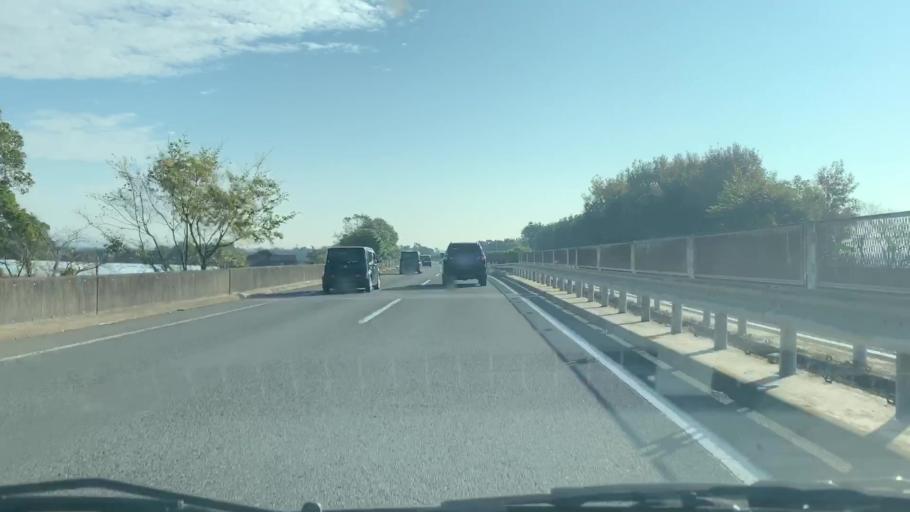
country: JP
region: Saga Prefecture
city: Saga-shi
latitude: 33.3071
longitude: 130.2305
